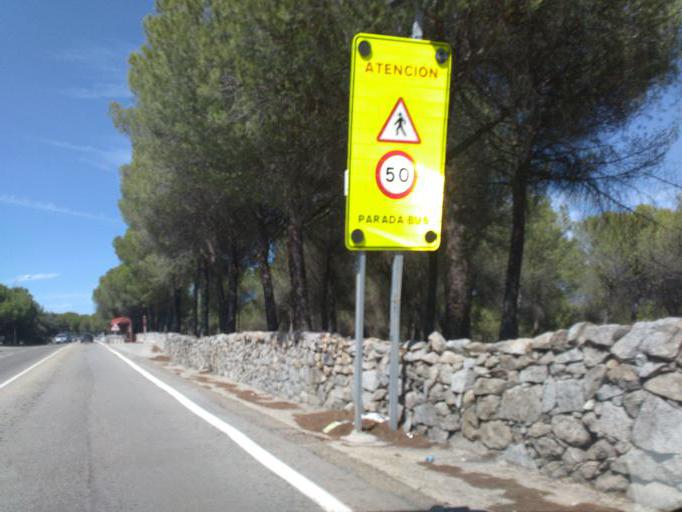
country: ES
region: Madrid
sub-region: Provincia de Madrid
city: Galapagar
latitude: 40.5621
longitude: -3.9690
